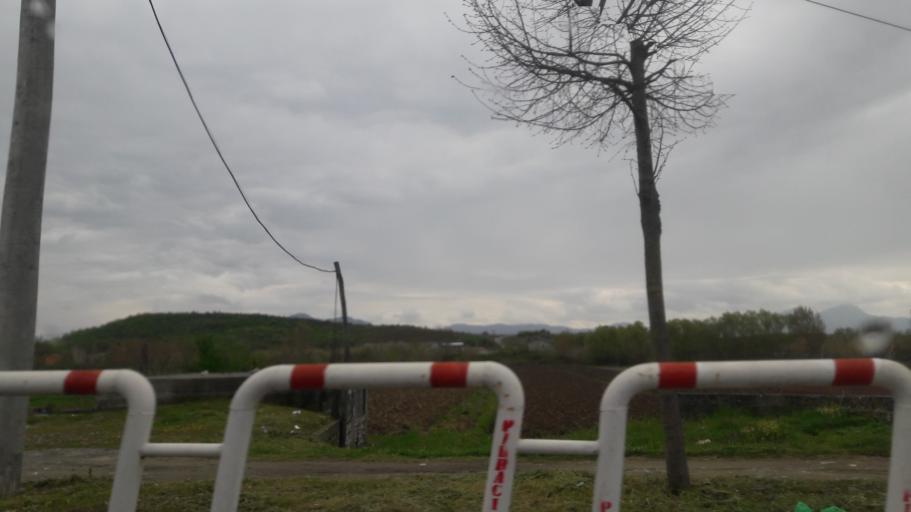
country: AL
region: Shkoder
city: Vukatane
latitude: 41.9616
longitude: 19.5367
